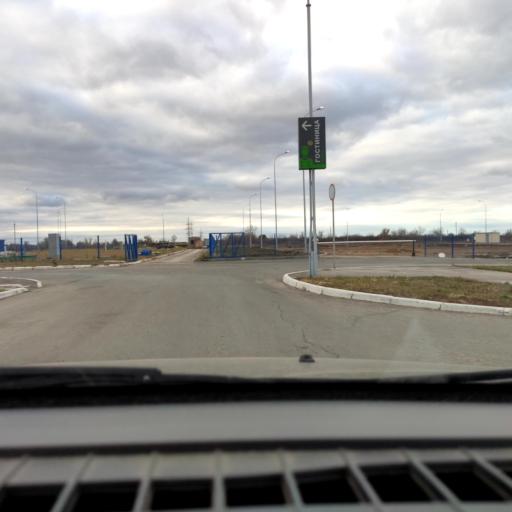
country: RU
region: Samara
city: Podstepki
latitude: 53.5556
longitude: 49.2141
